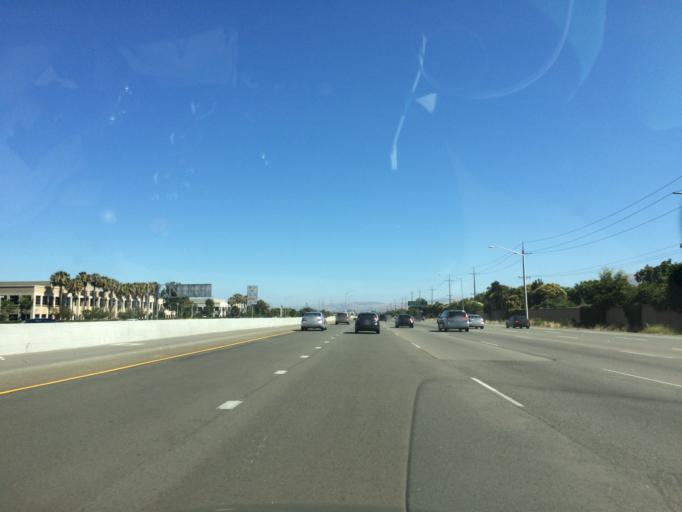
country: US
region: California
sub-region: Santa Clara County
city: Milpitas
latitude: 37.4369
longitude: -121.9194
